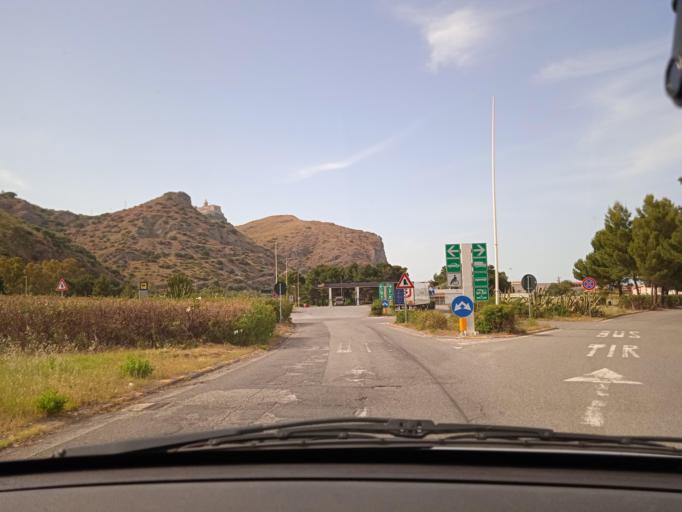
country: IT
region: Sicily
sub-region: Messina
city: Oliveri
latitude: 38.1267
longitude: 15.0539
